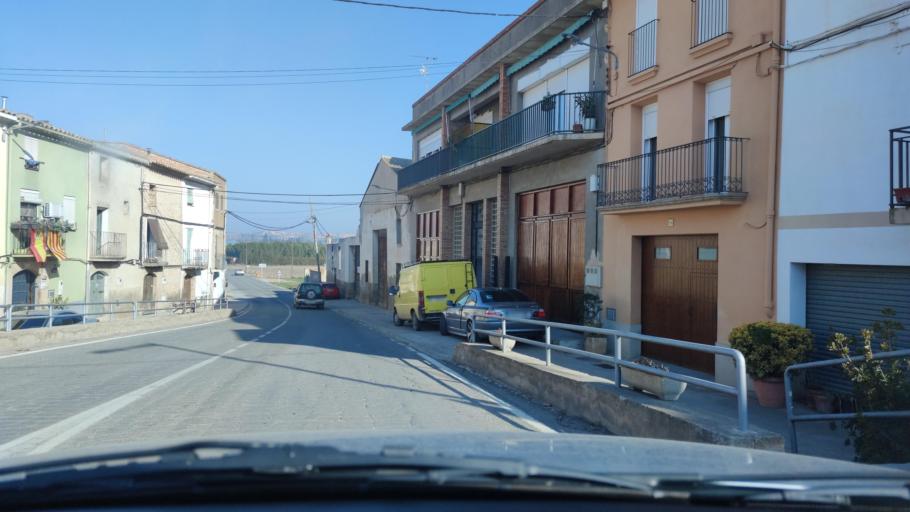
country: ES
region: Catalonia
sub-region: Provincia de Lleida
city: Aspa
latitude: 41.5447
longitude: 0.7346
